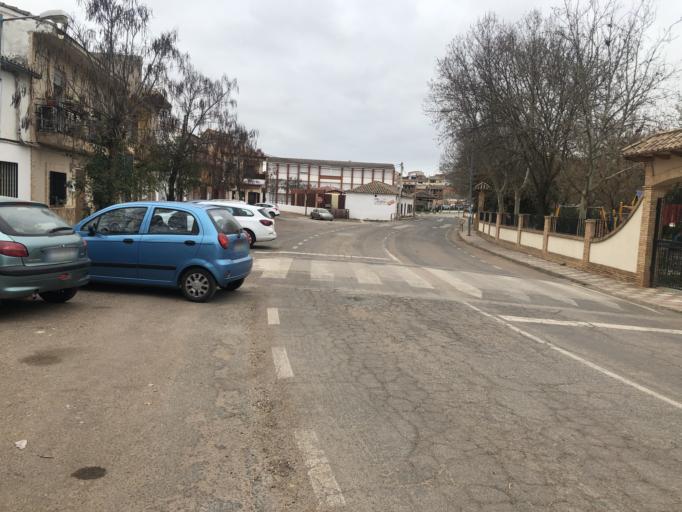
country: ES
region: Castille-La Mancha
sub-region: Provincia de Ciudad Real
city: Navalpino
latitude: 39.3273
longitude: -4.6497
